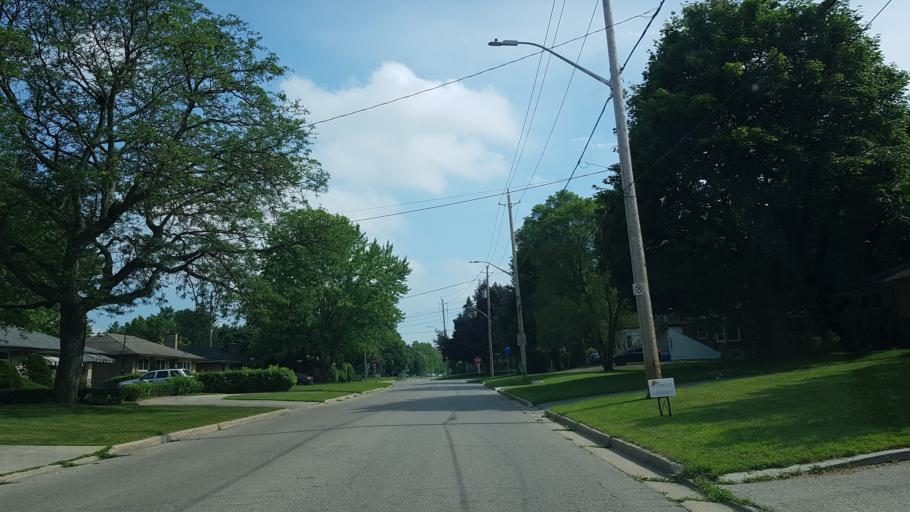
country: CA
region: Ontario
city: Delaware
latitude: 42.9603
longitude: -81.3422
